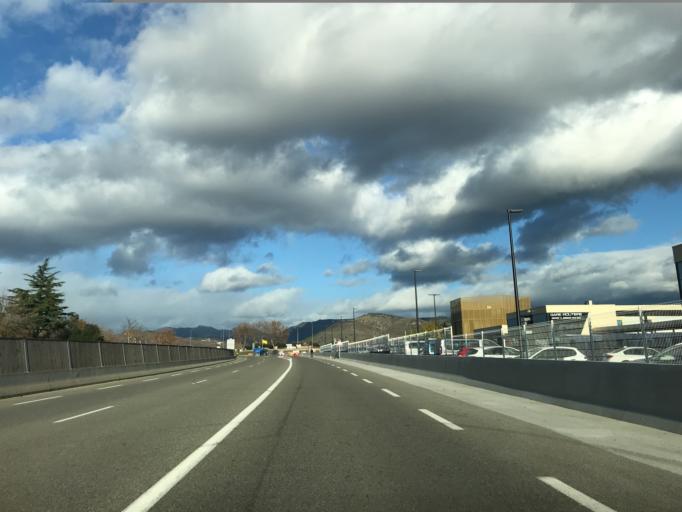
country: FR
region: Rhone-Alpes
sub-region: Departement de l'Ardeche
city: Aubenas
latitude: 44.6106
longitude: 4.4059
